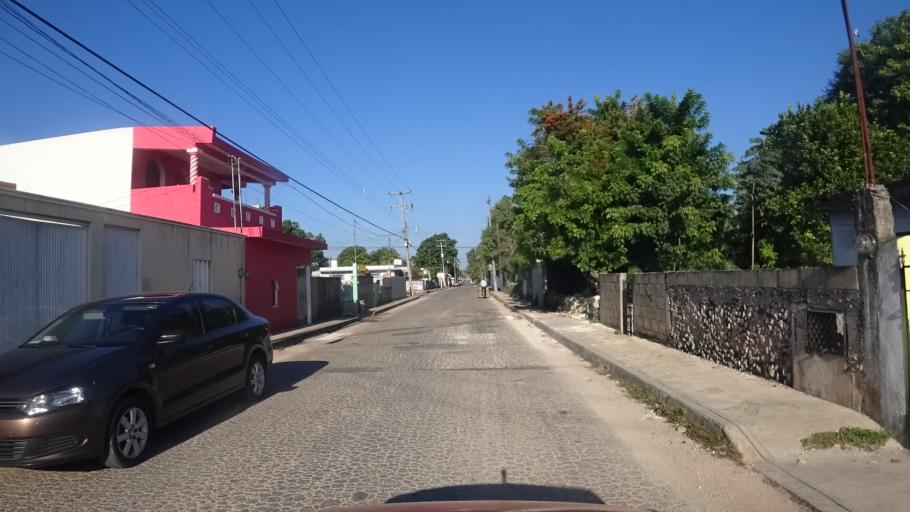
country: MX
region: Yucatan
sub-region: Tizimin
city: Tizimin
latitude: 21.1542
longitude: -88.1564
